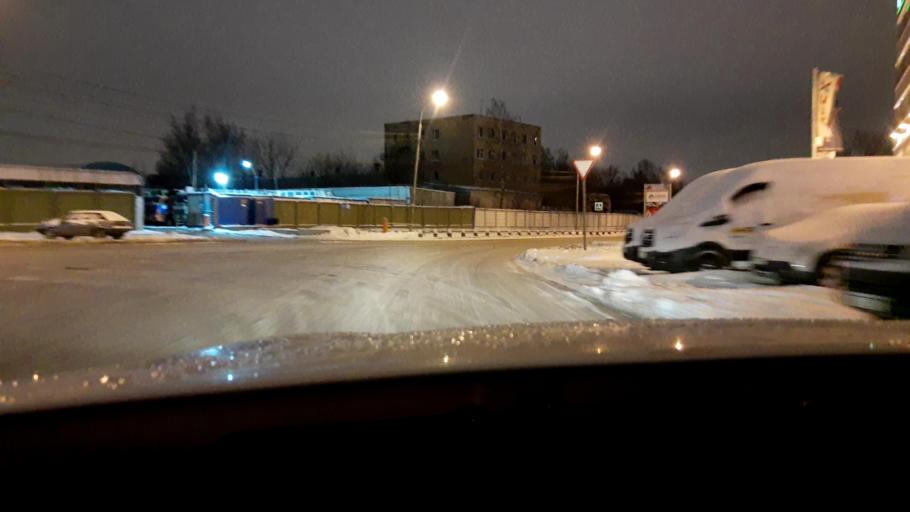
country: RU
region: Moscow
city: Khimki
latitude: 55.9121
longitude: 37.4193
